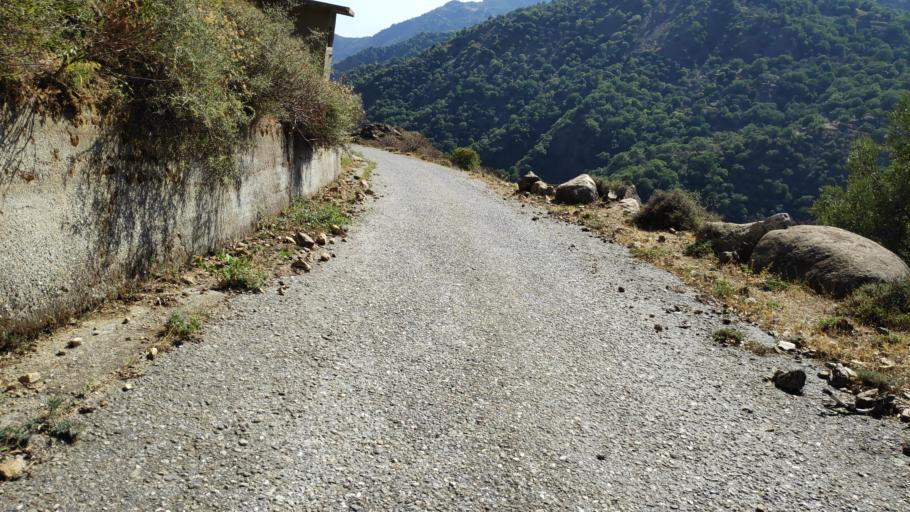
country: IT
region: Calabria
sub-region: Provincia di Reggio Calabria
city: Roccaforte del Greco
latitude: 38.0520
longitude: 15.9187
